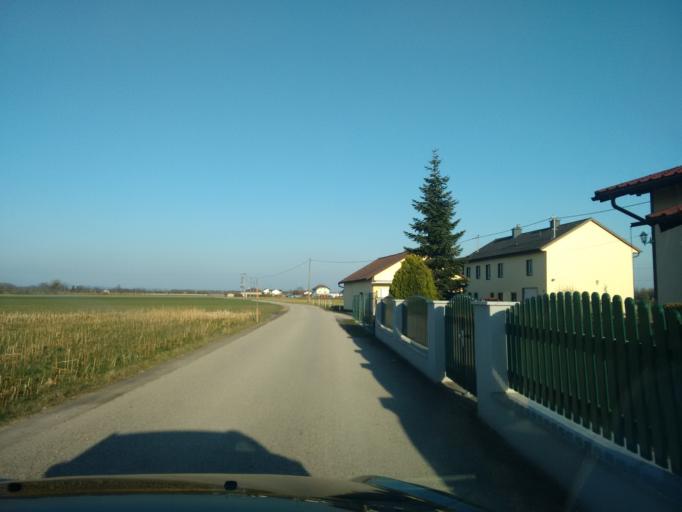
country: AT
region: Upper Austria
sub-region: Wels-Land
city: Marchtrenk
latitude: 48.2045
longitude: 14.1257
